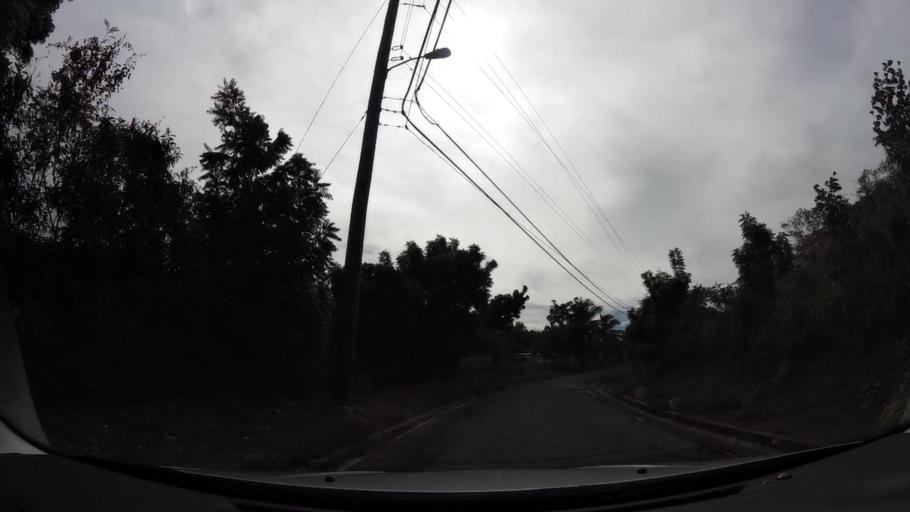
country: AG
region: Saint Peter
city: Parham
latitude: 17.0616
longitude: -61.7247
